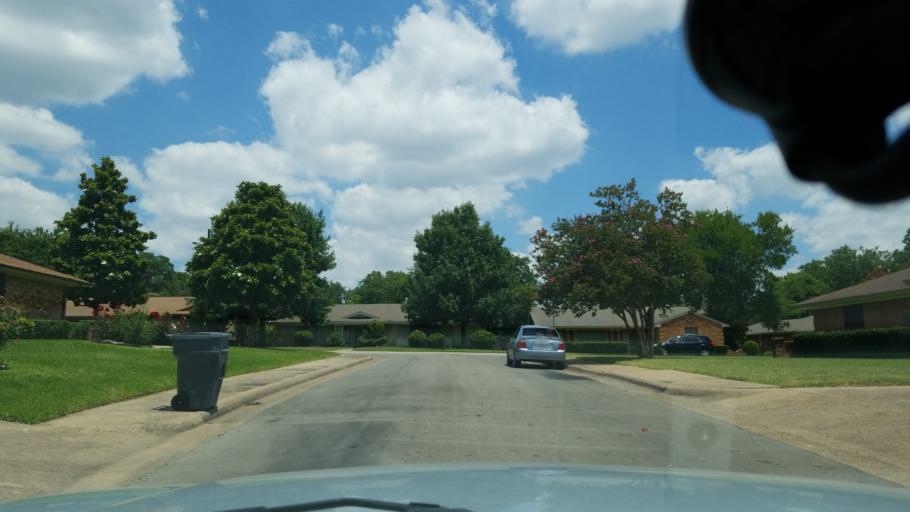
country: US
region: Texas
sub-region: Dallas County
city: Cockrell Hill
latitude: 32.6931
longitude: -96.8768
